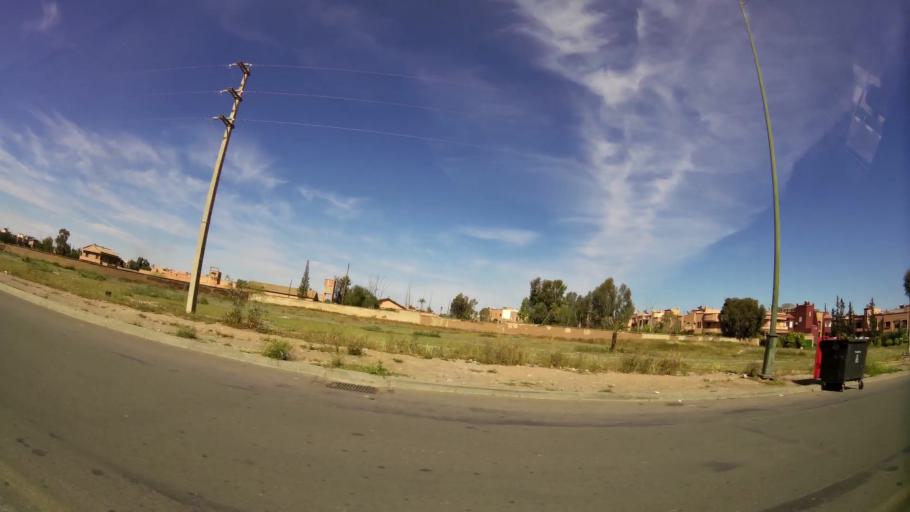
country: MA
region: Marrakech-Tensift-Al Haouz
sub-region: Marrakech
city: Marrakesh
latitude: 31.6522
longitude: -8.0504
